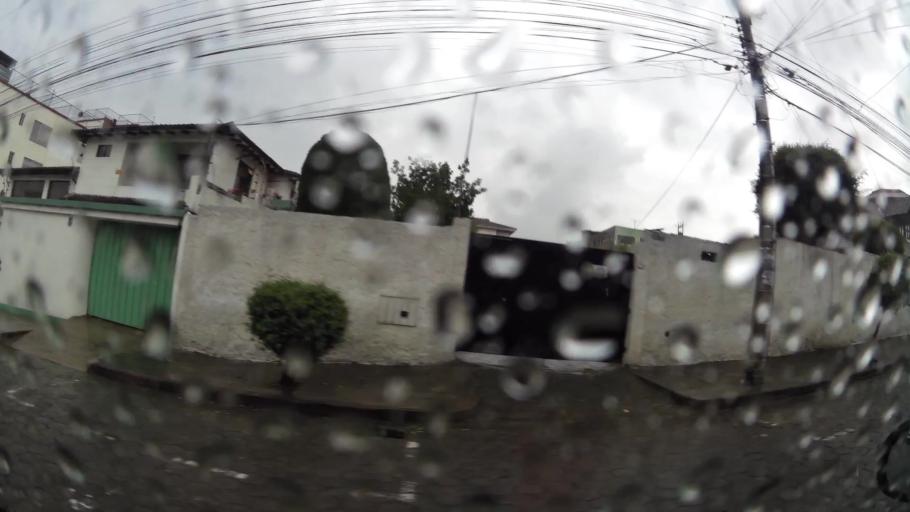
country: EC
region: Pichincha
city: Quito
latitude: -0.1557
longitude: -78.4617
